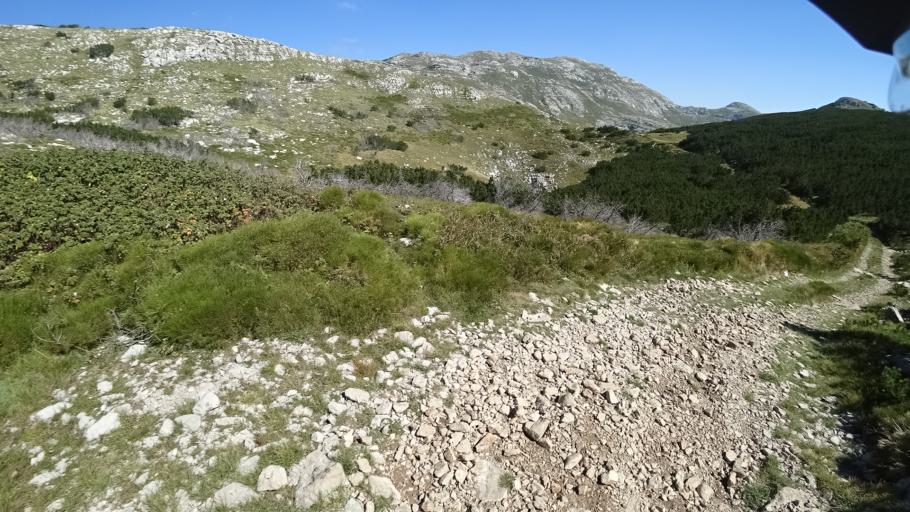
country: HR
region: Splitsko-Dalmatinska
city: Hrvace
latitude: 43.9367
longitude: 16.5727
